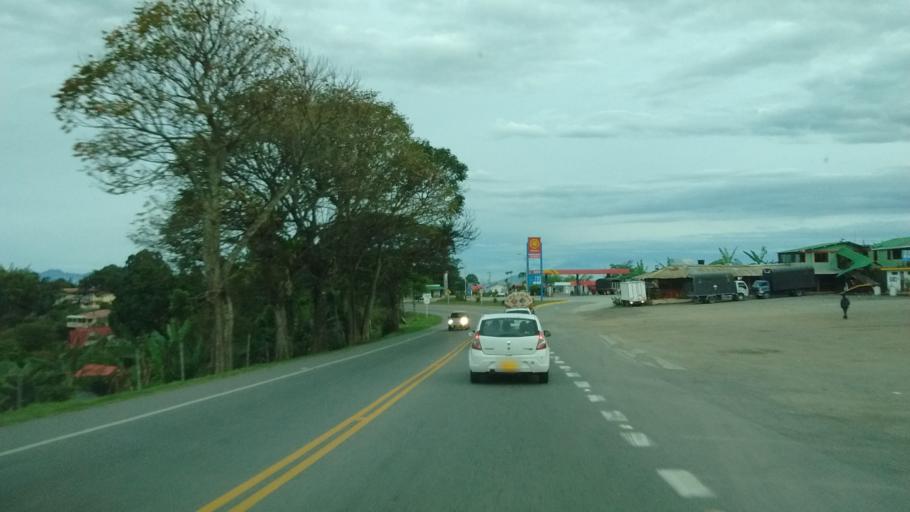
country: CO
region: Cauca
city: Cajibio
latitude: 2.6979
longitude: -76.5334
